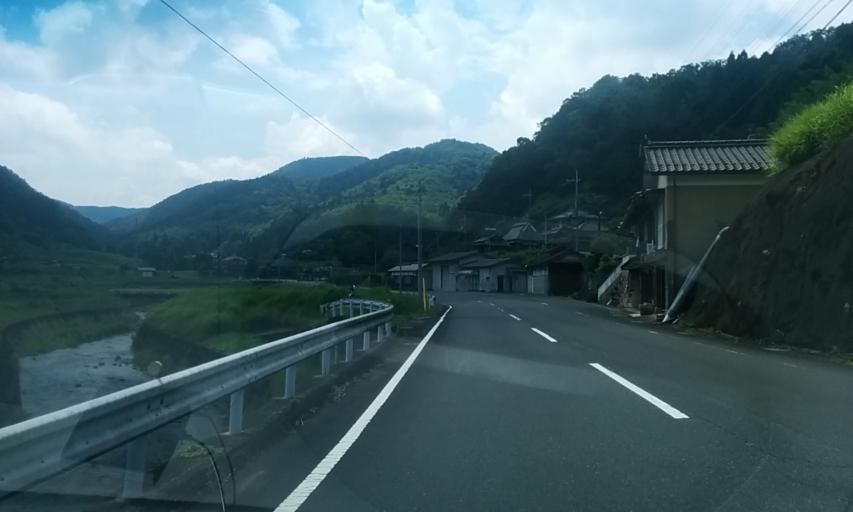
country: JP
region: Kyoto
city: Ayabe
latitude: 35.1955
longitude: 135.2175
